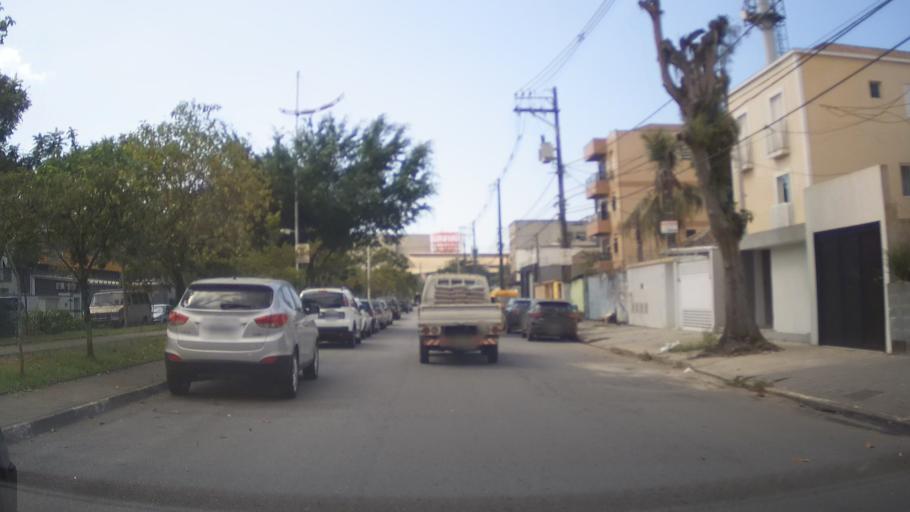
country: BR
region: Sao Paulo
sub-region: Santos
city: Santos
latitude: -23.9777
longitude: -46.2963
